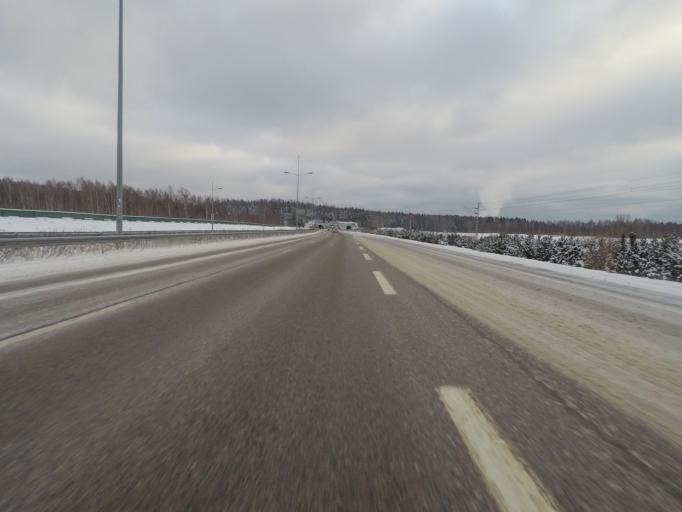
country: FI
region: Uusimaa
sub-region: Helsinki
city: Vantaa
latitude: 60.2424
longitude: 25.1509
